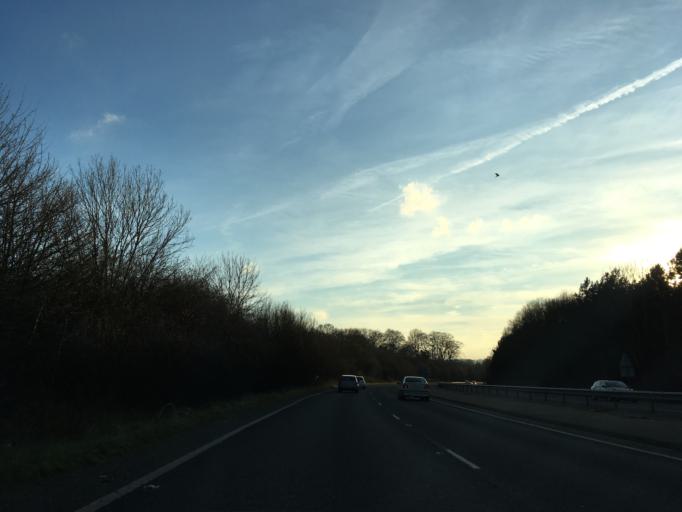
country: GB
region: England
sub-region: Borough of Stockport
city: Cheadle Hulme
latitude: 53.3444
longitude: -2.1995
